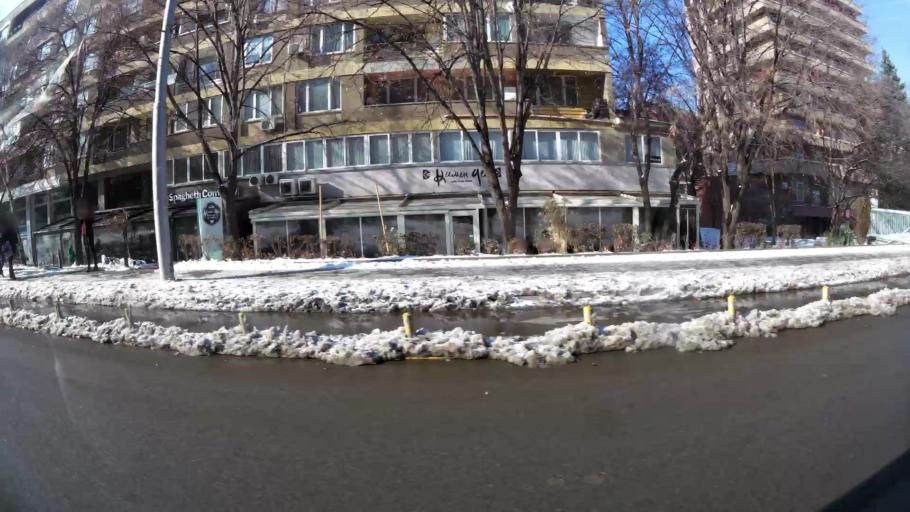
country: BG
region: Sofia-Capital
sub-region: Stolichna Obshtina
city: Sofia
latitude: 42.6801
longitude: 23.3116
